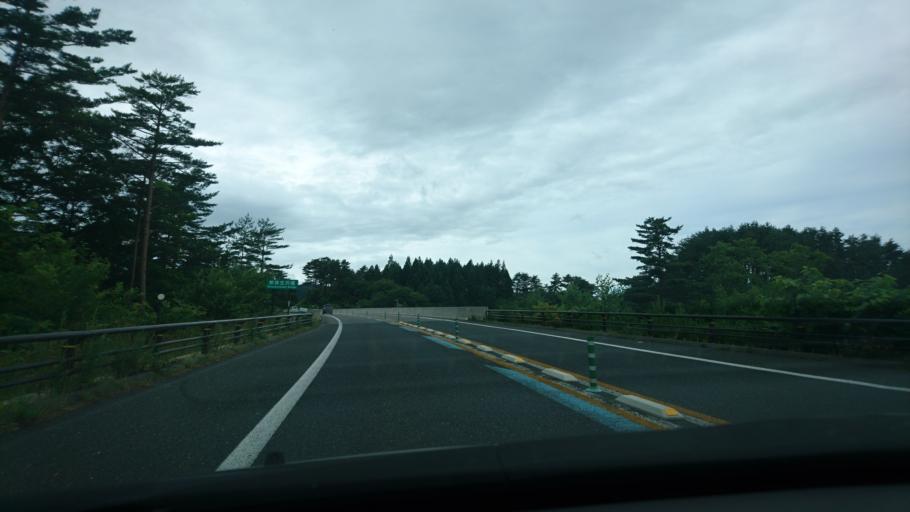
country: JP
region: Iwate
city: Miyako
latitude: 39.8756
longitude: 141.9353
